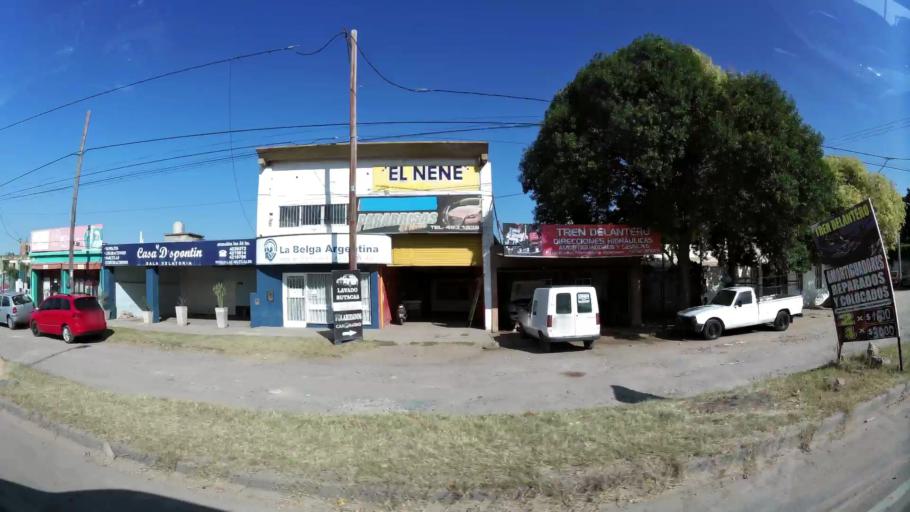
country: AR
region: Cordoba
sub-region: Departamento de Capital
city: Cordoba
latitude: -31.4682
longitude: -64.2255
